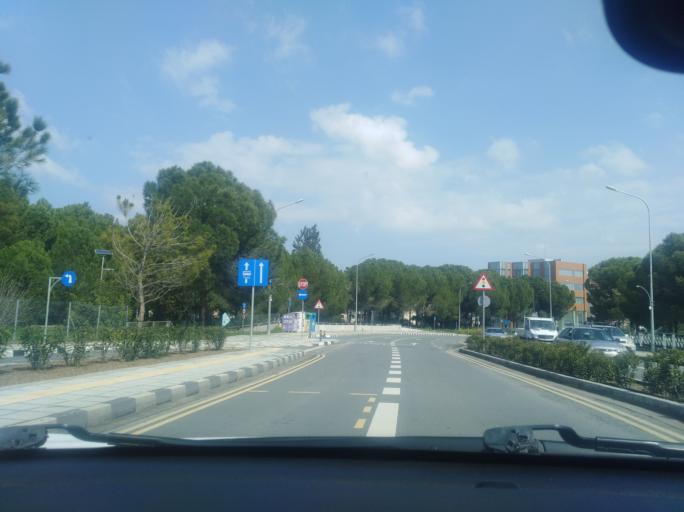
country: CY
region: Lefkosia
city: Nicosia
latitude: 35.1566
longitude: 33.3833
